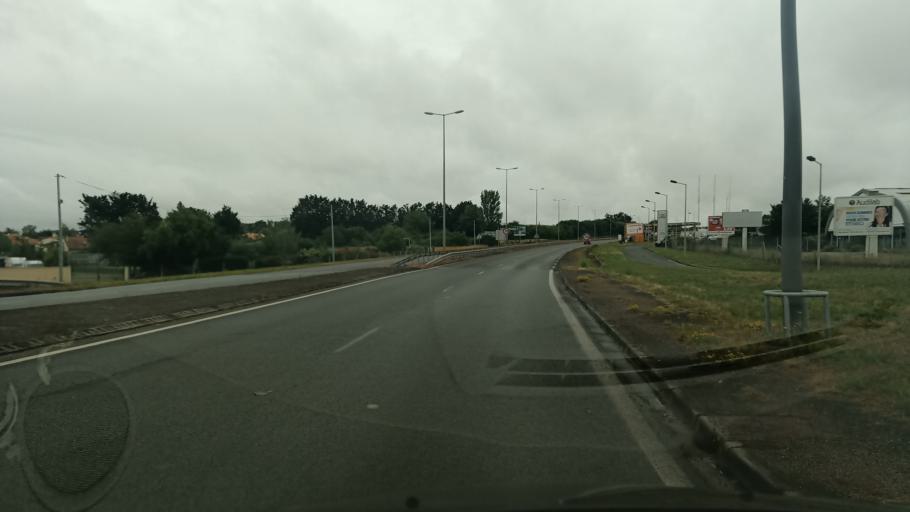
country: FR
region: Poitou-Charentes
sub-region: Departement de la Vienne
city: Poitiers
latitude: 46.6052
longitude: 0.3349
